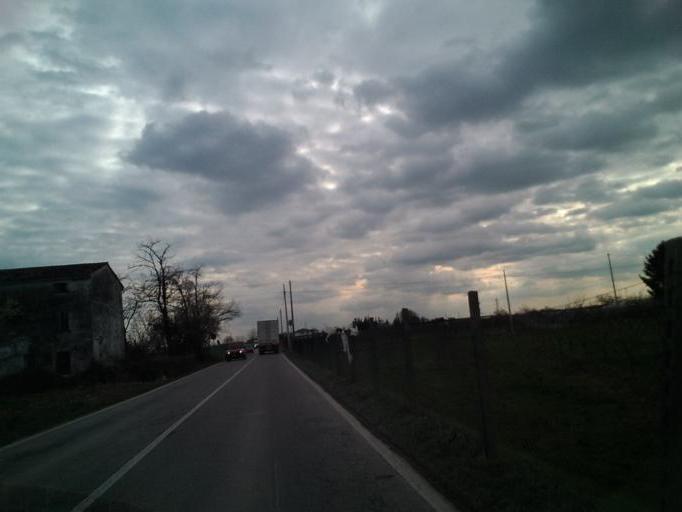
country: IT
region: Veneto
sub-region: Provincia di Verona
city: Alpo
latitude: 45.3917
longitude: 10.9359
